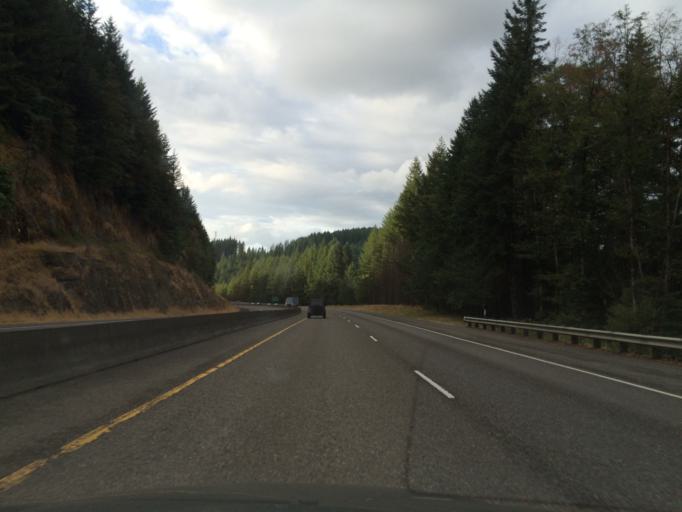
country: US
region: Oregon
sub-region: Douglas County
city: Drain
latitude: 43.7011
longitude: -123.2037
